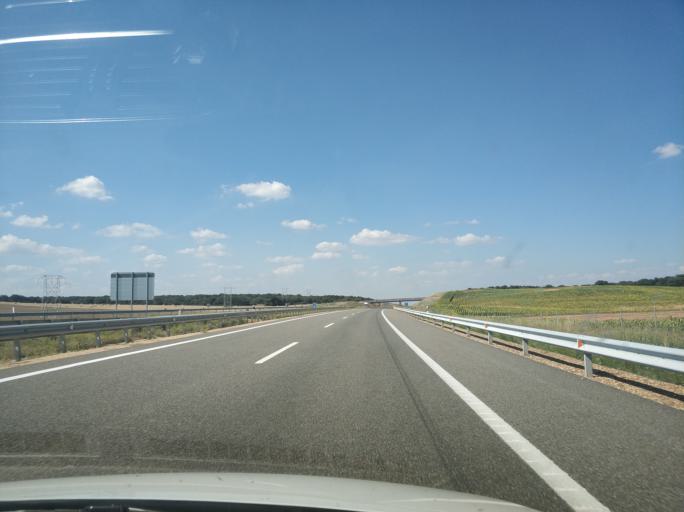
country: ES
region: Castille and Leon
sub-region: Provincia de Zamora
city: Granja de Moreruela
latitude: 41.8383
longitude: -5.7420
